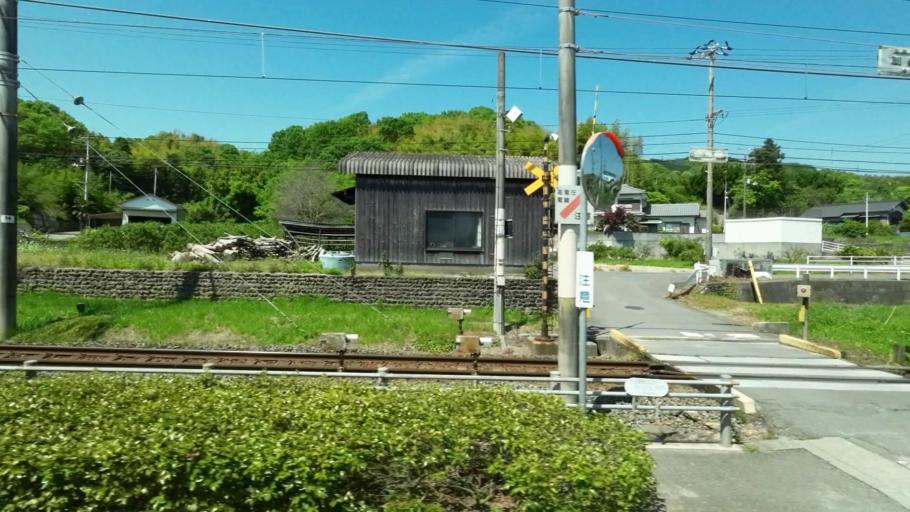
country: JP
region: Ehime
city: Hojo
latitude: 34.0823
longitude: 132.9845
